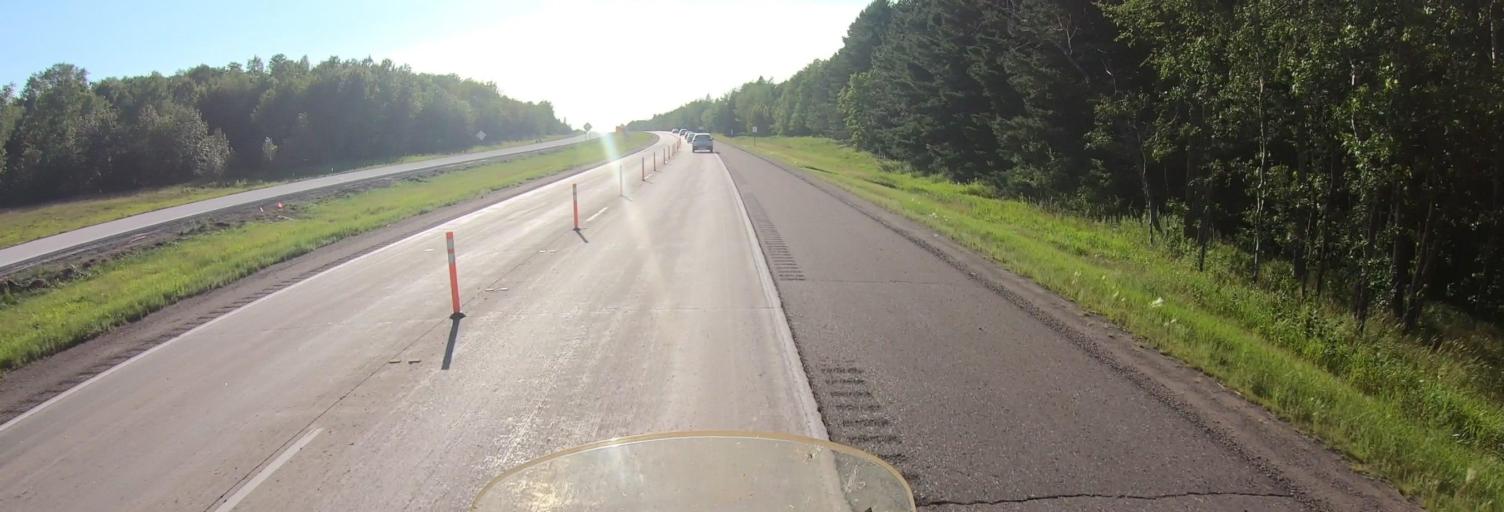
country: US
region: Minnesota
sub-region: Saint Louis County
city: Hermantown
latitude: 46.8521
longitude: -92.2905
